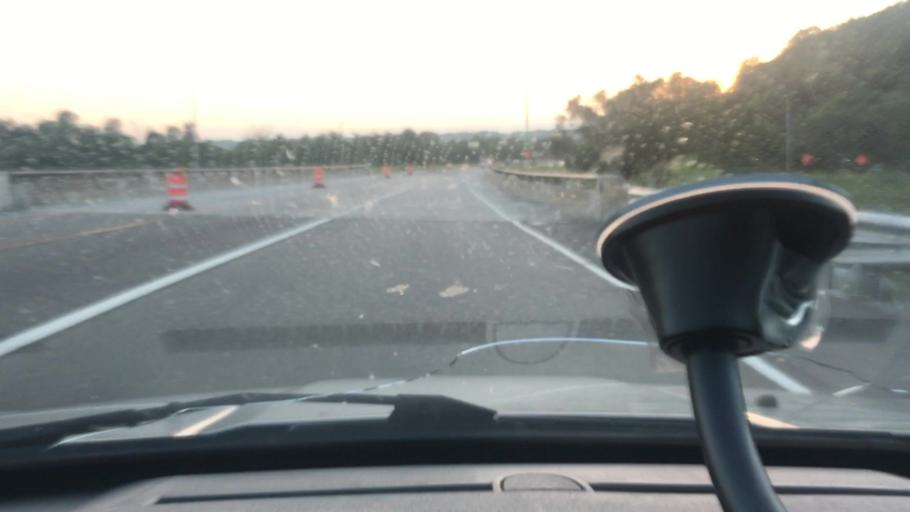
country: US
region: Illinois
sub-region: Tazewell County
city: Marquette Heights
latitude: 40.6301
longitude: -89.6124
